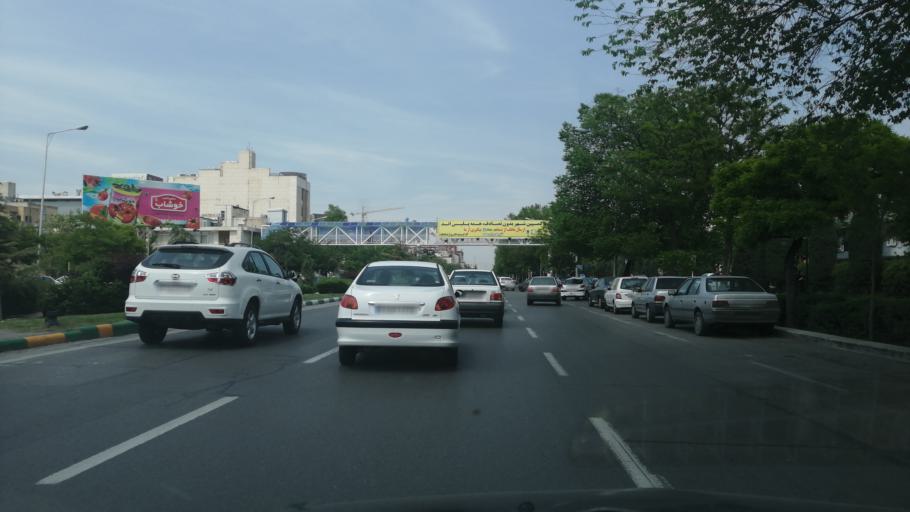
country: IR
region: Razavi Khorasan
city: Mashhad
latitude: 36.3096
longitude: 59.5548
